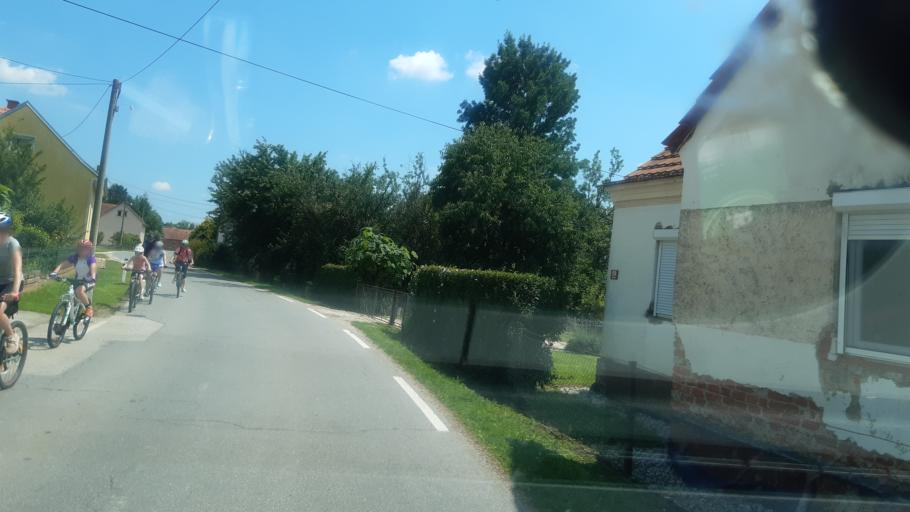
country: SI
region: Beltinci
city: Gancani
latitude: 46.6581
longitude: 16.2512
